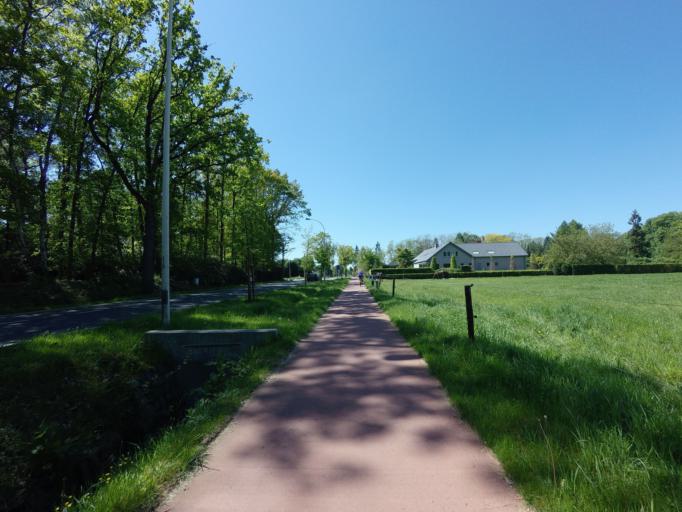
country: BE
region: Flanders
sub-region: Provincie Antwerpen
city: Essen
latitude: 51.4562
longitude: 4.4367
